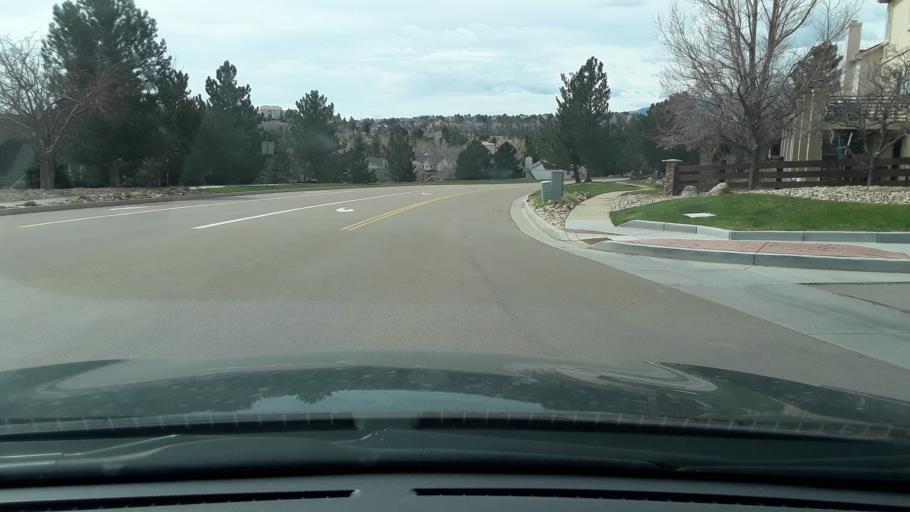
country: US
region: Colorado
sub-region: El Paso County
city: Air Force Academy
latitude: 38.9530
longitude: -104.8632
